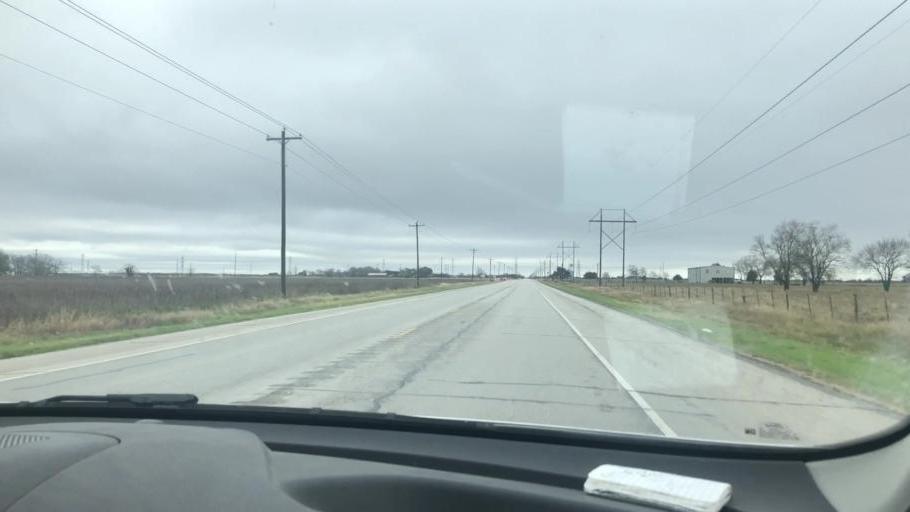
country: US
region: Texas
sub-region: Wharton County
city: Boling
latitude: 29.1887
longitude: -96.0132
